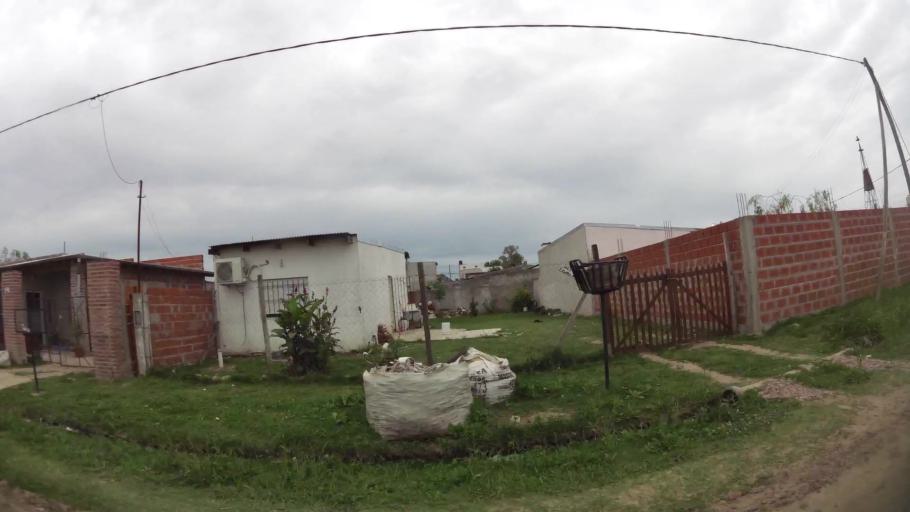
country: AR
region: Buenos Aires
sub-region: Partido de Zarate
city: Zarate
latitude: -34.1180
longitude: -59.0328
